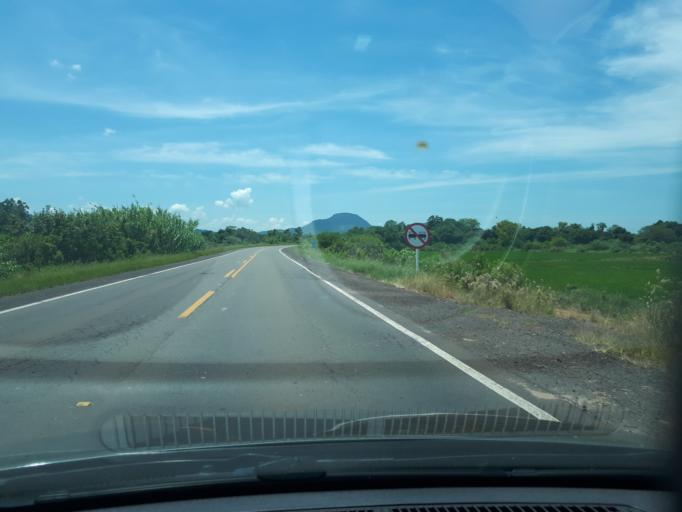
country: BR
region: Rio Grande do Sul
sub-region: Candelaria
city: Candelaria
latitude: -29.7256
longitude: -52.9300
